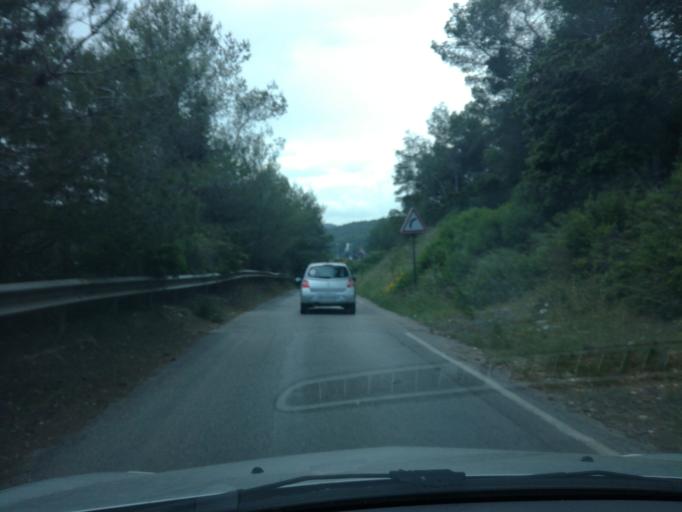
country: FR
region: Provence-Alpes-Cote d'Azur
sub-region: Departement des Alpes-Maritimes
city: Vallauris
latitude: 43.6042
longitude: 7.0711
